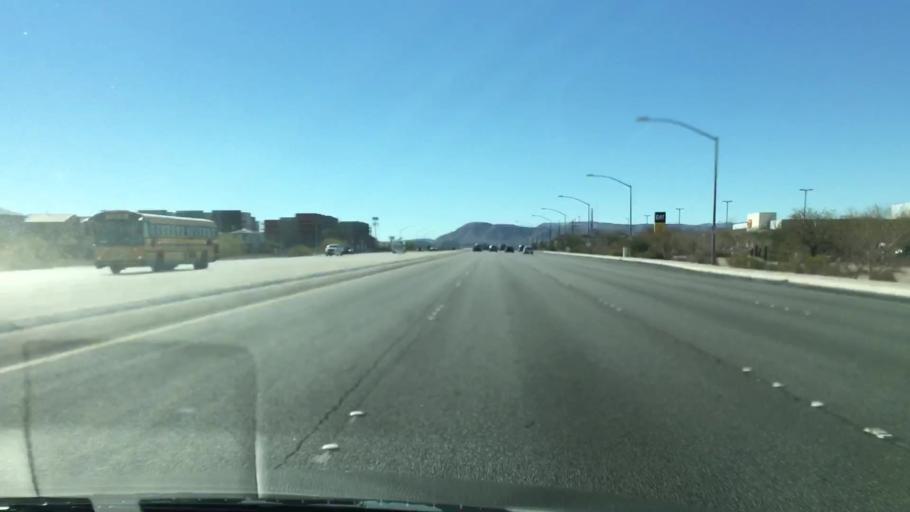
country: US
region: Nevada
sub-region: Clark County
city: Whitney
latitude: 35.9965
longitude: -115.1299
